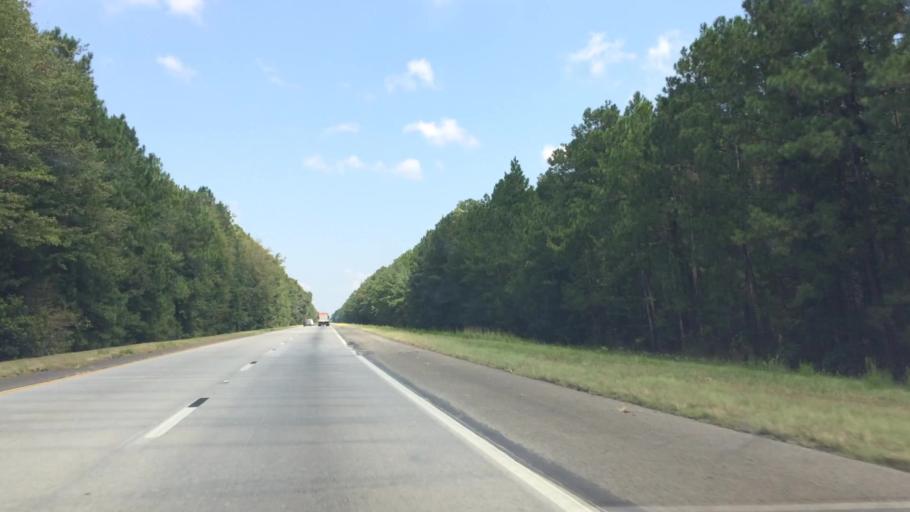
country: US
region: South Carolina
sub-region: Colleton County
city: Walterboro
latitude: 33.0498
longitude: -80.6678
